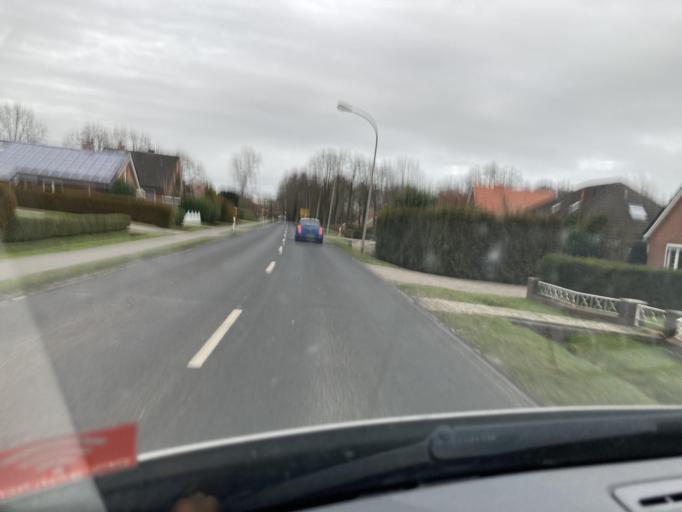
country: DE
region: Lower Saxony
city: Papenburg
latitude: 53.1307
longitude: 7.4726
